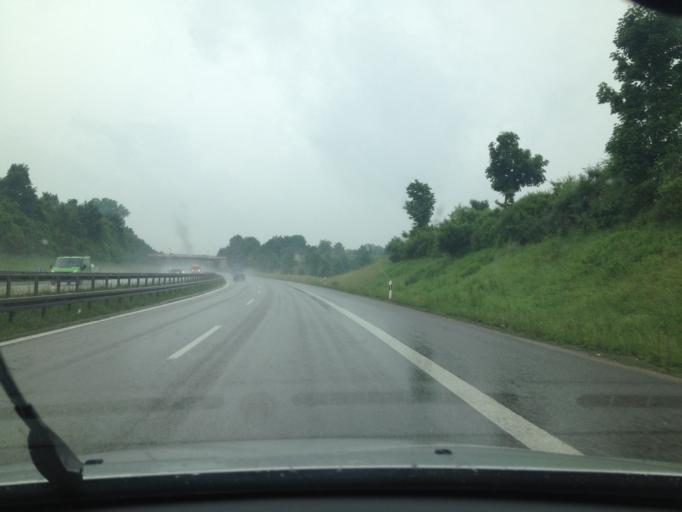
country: DE
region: Bavaria
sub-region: Swabia
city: Klosterlechfeld
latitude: 48.1585
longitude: 10.8403
